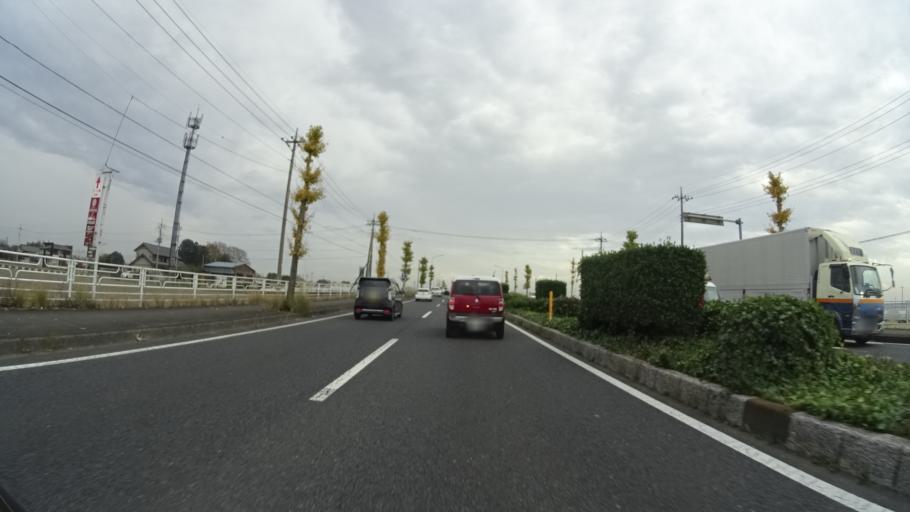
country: JP
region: Gunma
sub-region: Sawa-gun
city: Tamamura
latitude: 36.3698
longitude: 139.1456
